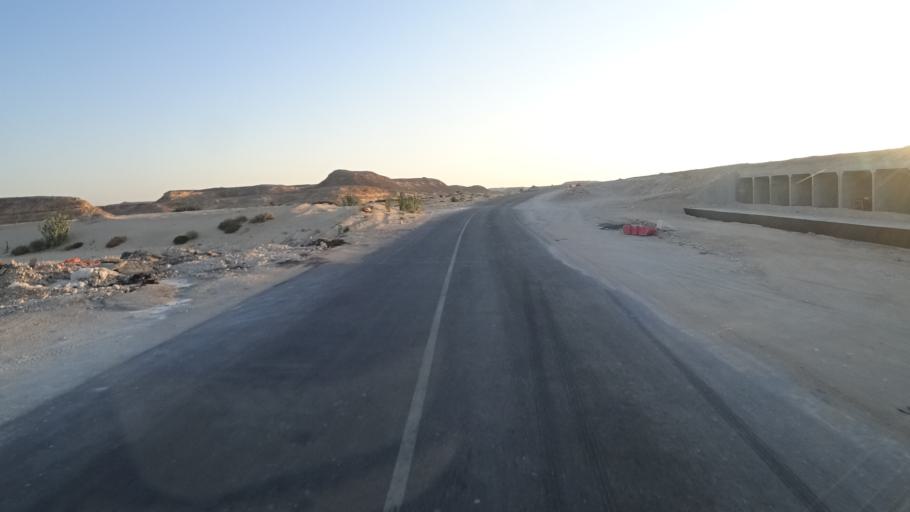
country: OM
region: Zufar
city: Salalah
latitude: 17.5171
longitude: 53.3748
